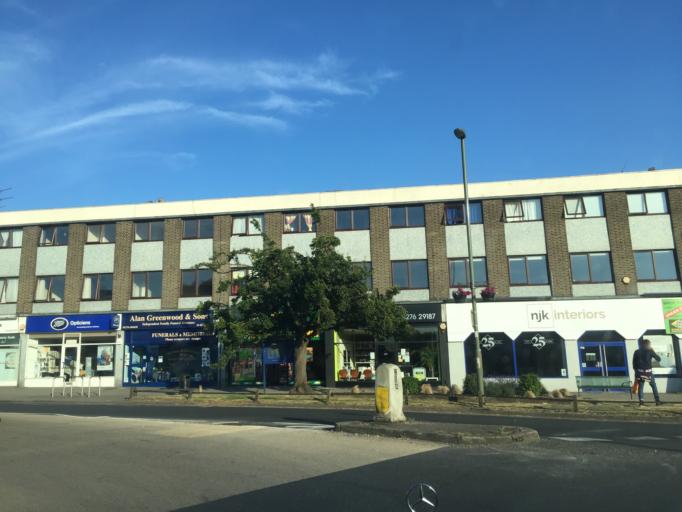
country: GB
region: England
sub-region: Surrey
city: Frimley
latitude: 51.3144
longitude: -0.7436
